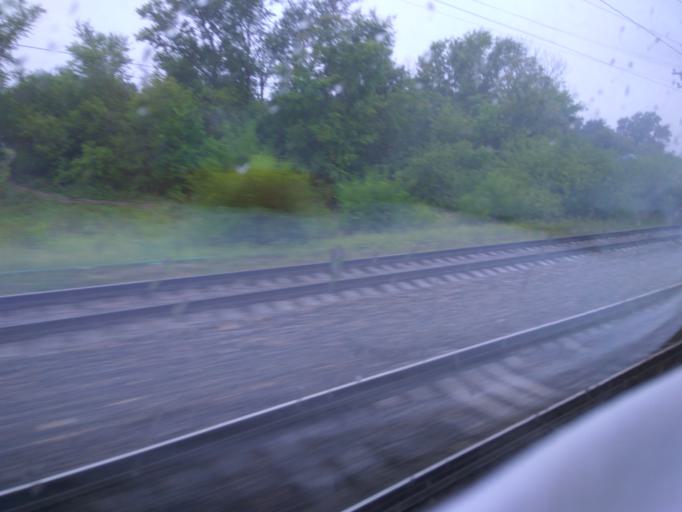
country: RU
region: Moskovskaya
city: Uzunovo
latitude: 54.6774
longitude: 38.5316
